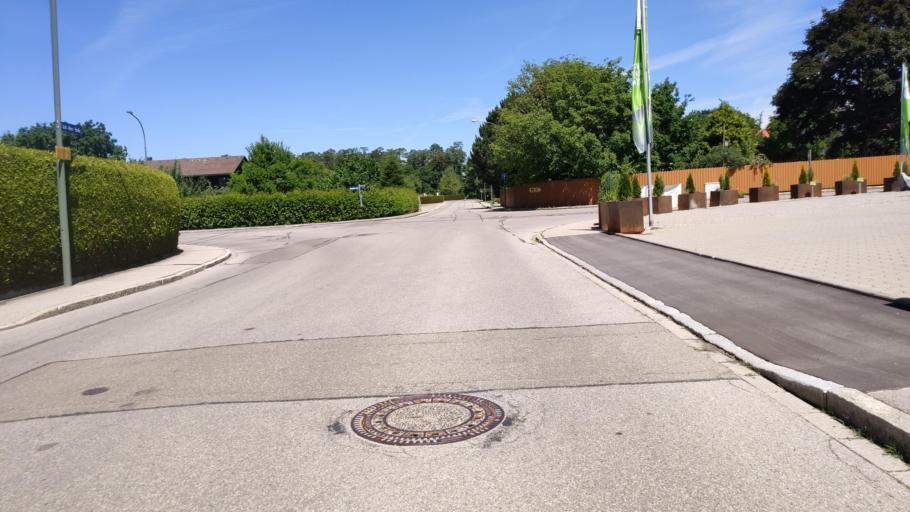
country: DE
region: Bavaria
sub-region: Swabia
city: Bad Worishofen
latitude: 48.0234
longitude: 10.6017
